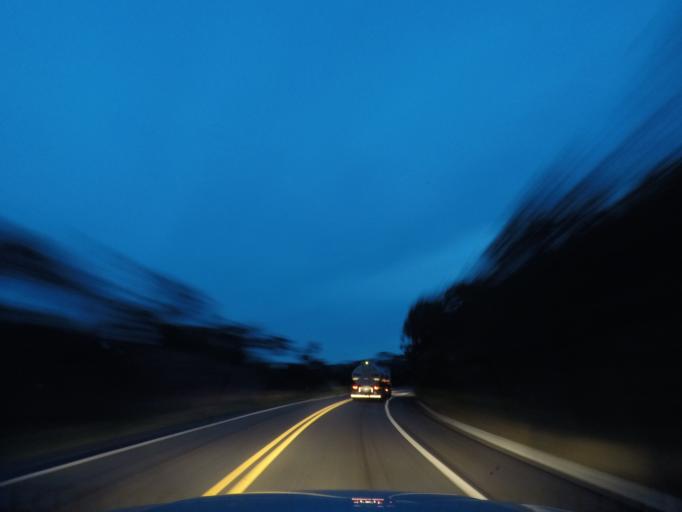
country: BR
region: Bahia
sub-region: Andarai
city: Vera Cruz
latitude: -12.4989
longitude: -41.3300
